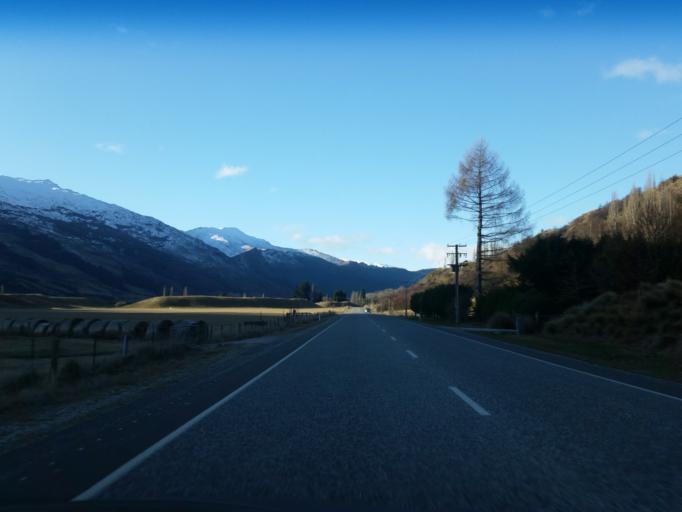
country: NZ
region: Otago
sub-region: Queenstown-Lakes District
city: Queenstown
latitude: -44.9660
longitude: 168.7110
